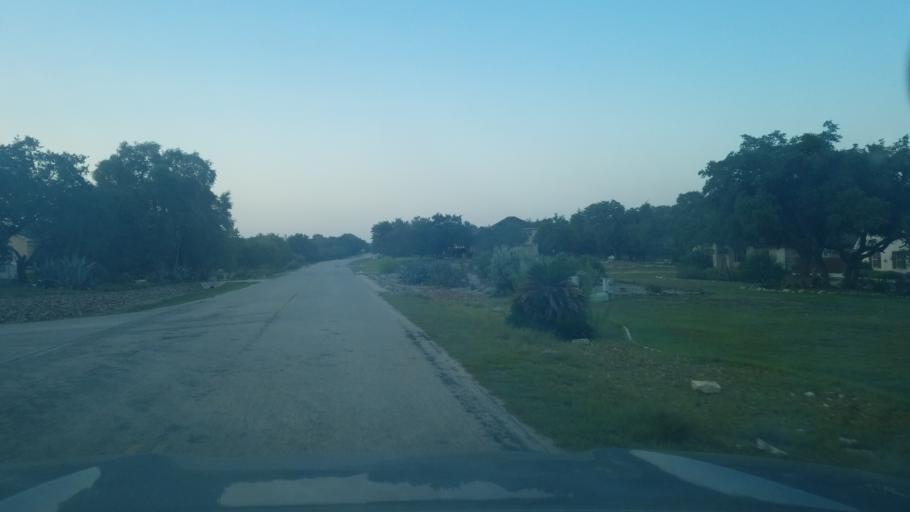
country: US
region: Texas
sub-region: Comal County
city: Bulverde
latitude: 29.8318
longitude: -98.4040
